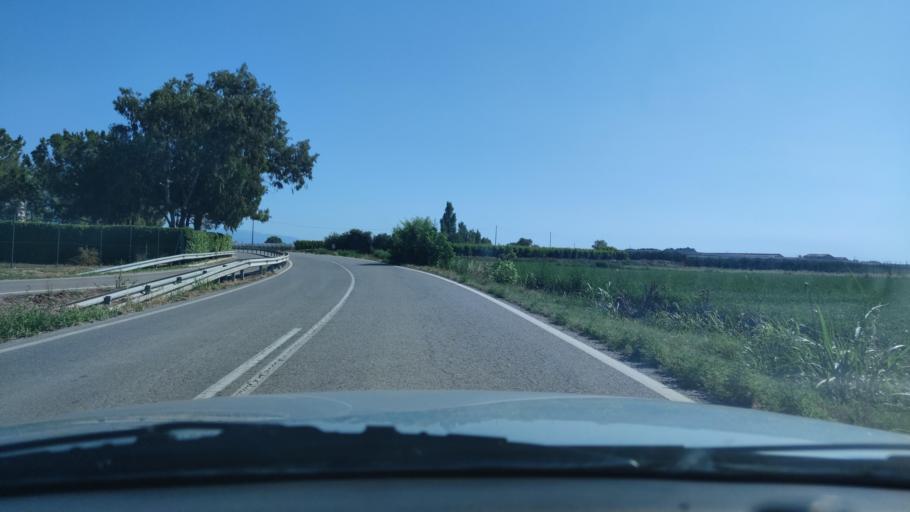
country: ES
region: Catalonia
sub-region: Provincia de Lleida
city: Bellvis
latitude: 41.6603
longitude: 0.8091
